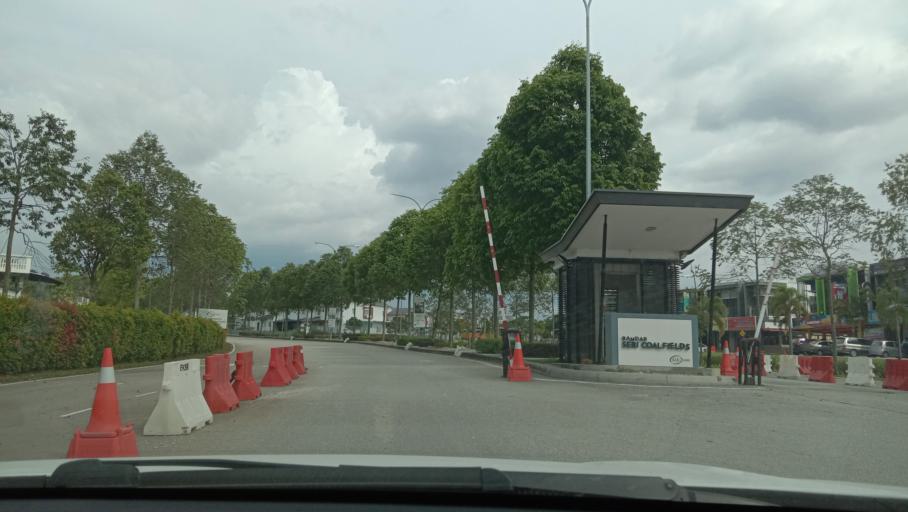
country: MY
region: Selangor
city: Ladang Seri Kundang
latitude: 3.2471
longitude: 101.4746
